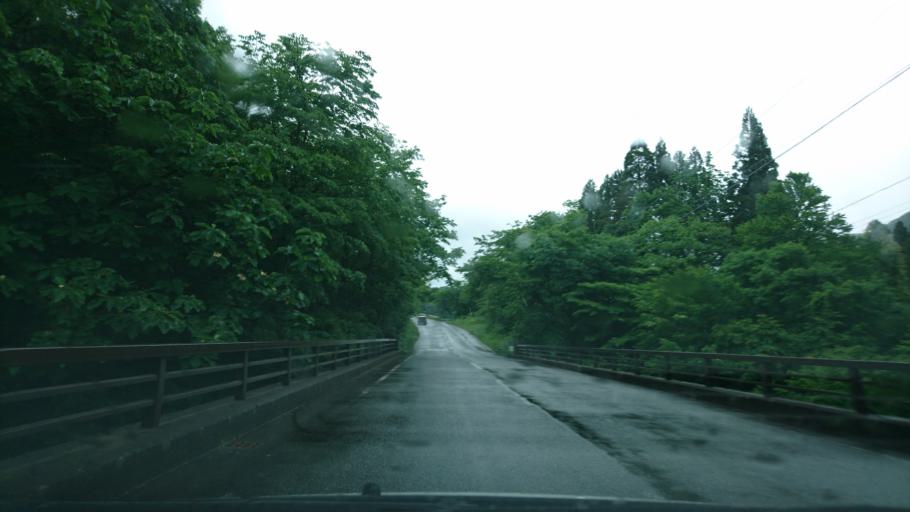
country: JP
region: Iwate
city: Ichinoseki
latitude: 38.9949
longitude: 140.9020
